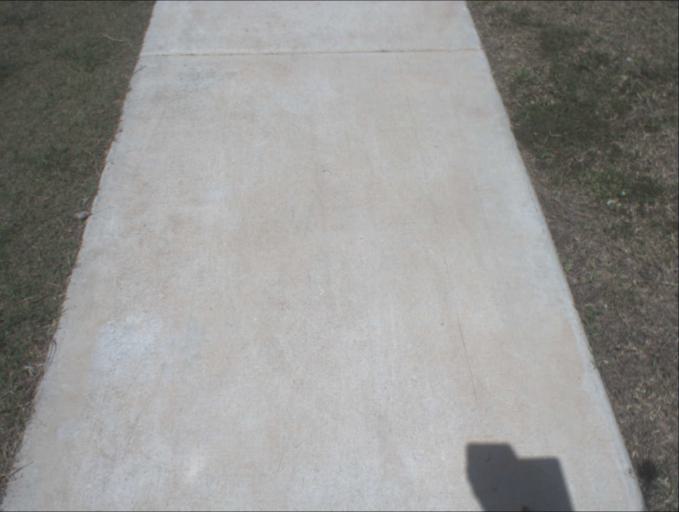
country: AU
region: Queensland
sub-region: Logan
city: Chambers Flat
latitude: -27.8005
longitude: 153.1108
